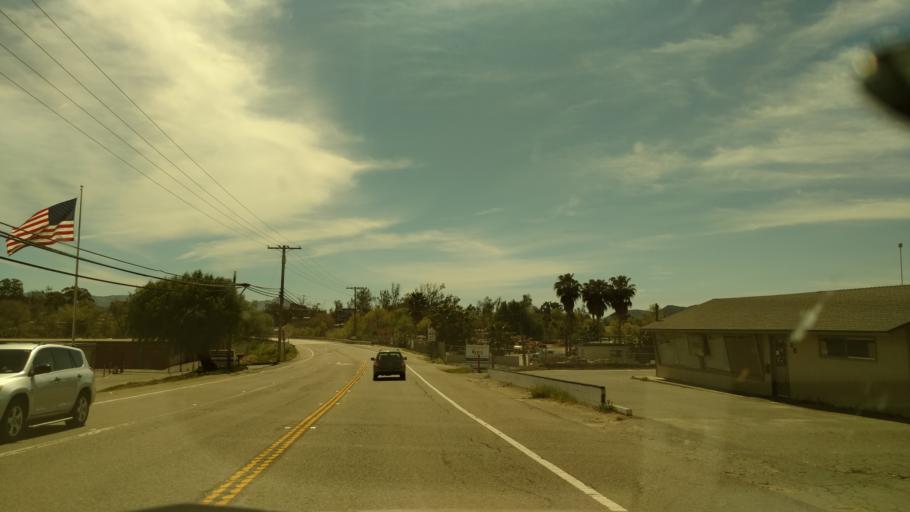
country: US
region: California
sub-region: San Diego County
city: Ramona
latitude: 33.0471
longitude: -116.8712
